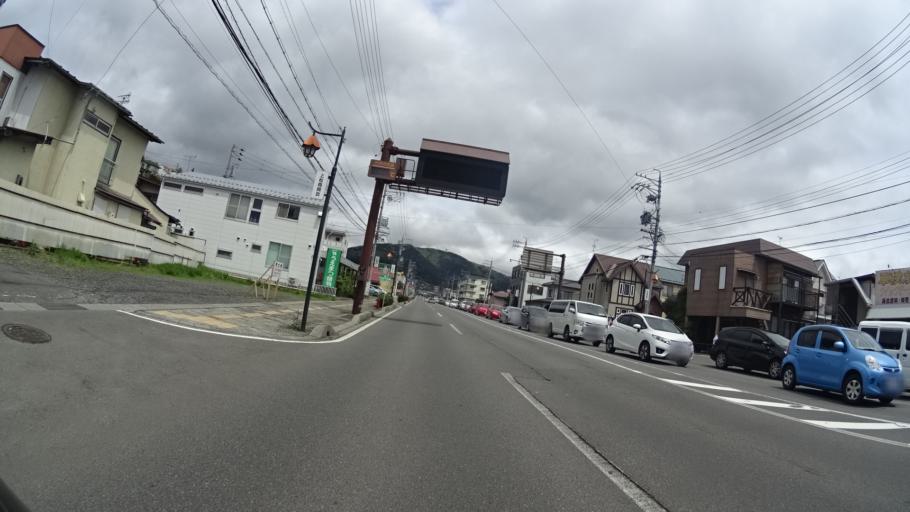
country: JP
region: Nagano
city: Nagano-shi
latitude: 36.6719
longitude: 138.1983
